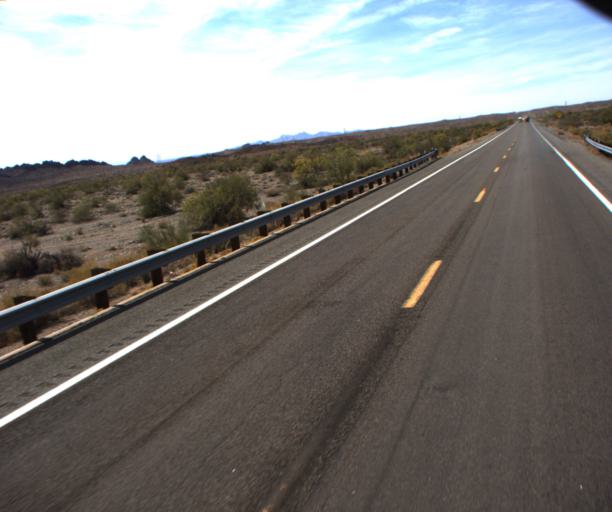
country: US
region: Arizona
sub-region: Mohave County
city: Lake Havasu City
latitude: 34.4115
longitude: -114.1907
